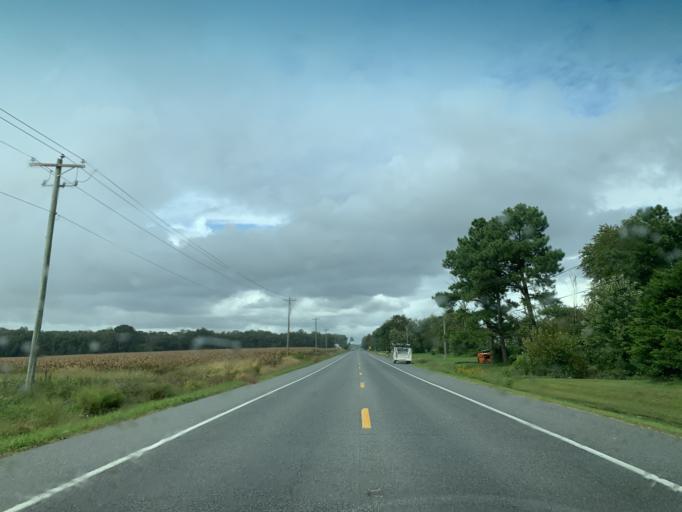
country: US
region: Maryland
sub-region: Caroline County
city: Ridgely
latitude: 38.9844
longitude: -75.8758
